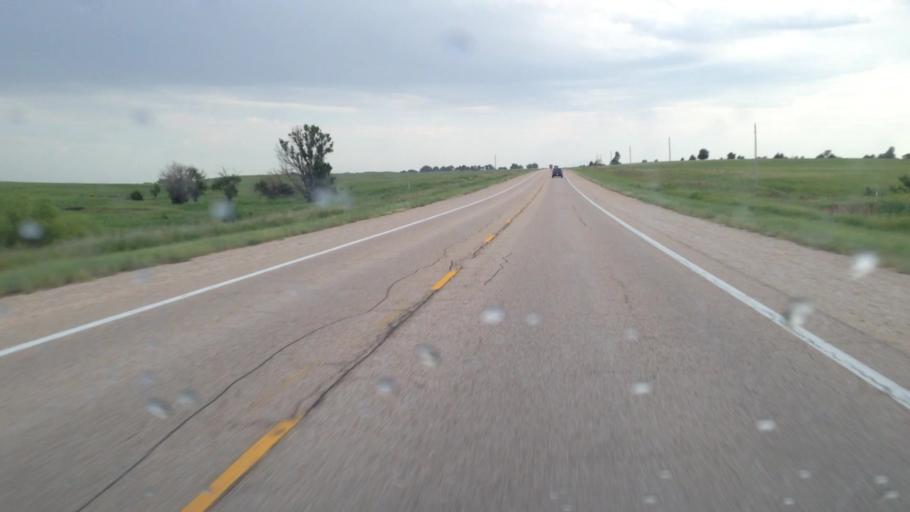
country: US
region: Kansas
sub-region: Coffey County
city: Burlington
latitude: 38.1540
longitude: -95.7388
